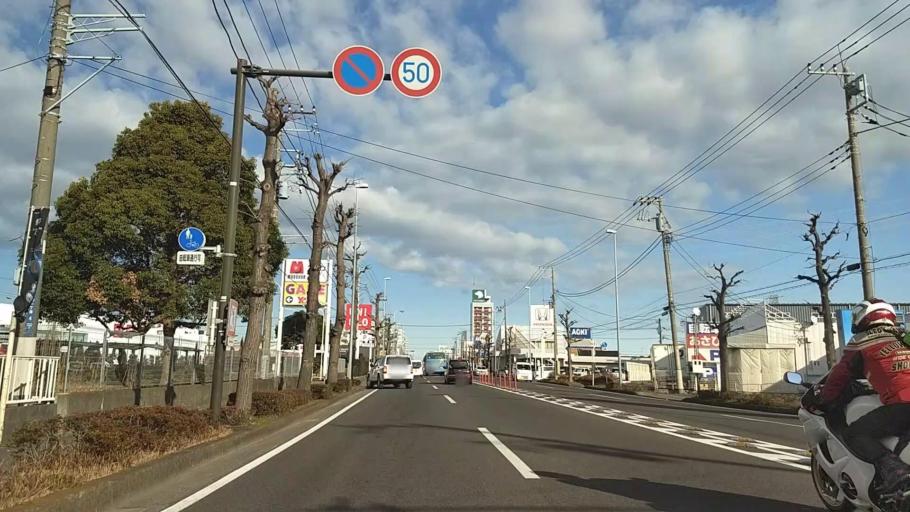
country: JP
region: Kanagawa
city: Hiratsuka
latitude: 35.3647
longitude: 139.3615
